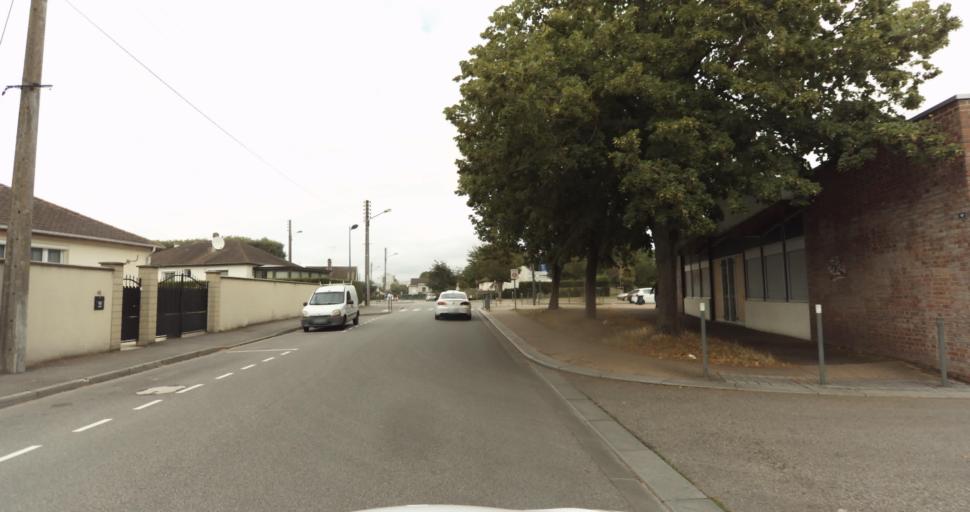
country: FR
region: Haute-Normandie
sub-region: Departement de l'Eure
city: Evreux
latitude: 49.0103
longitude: 1.1579
